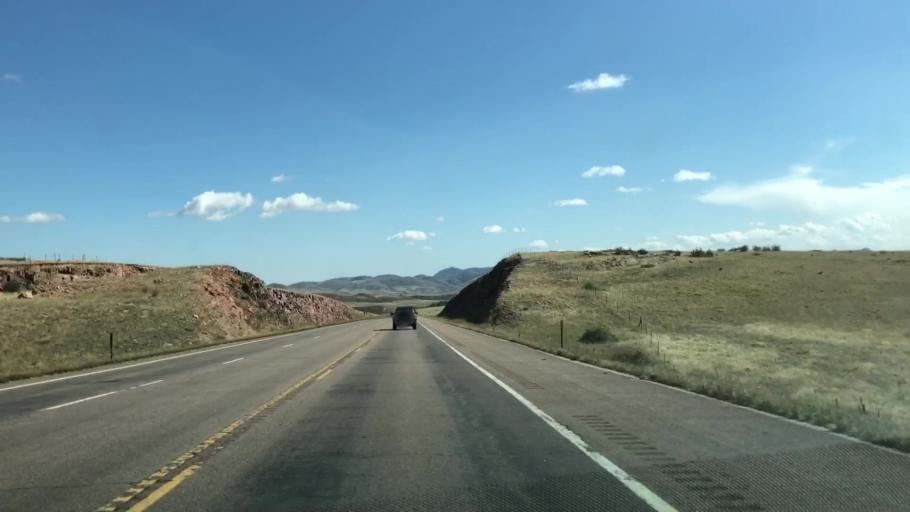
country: US
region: Colorado
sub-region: Larimer County
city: Laporte
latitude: 40.8447
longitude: -105.2530
